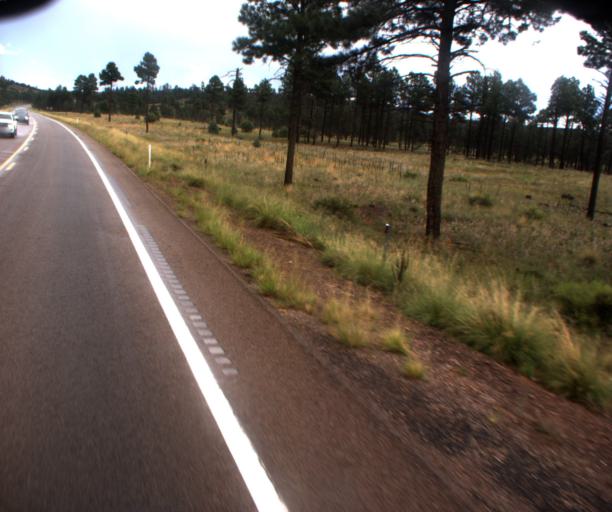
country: US
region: Arizona
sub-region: Navajo County
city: Heber-Overgaard
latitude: 34.3665
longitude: -110.4387
